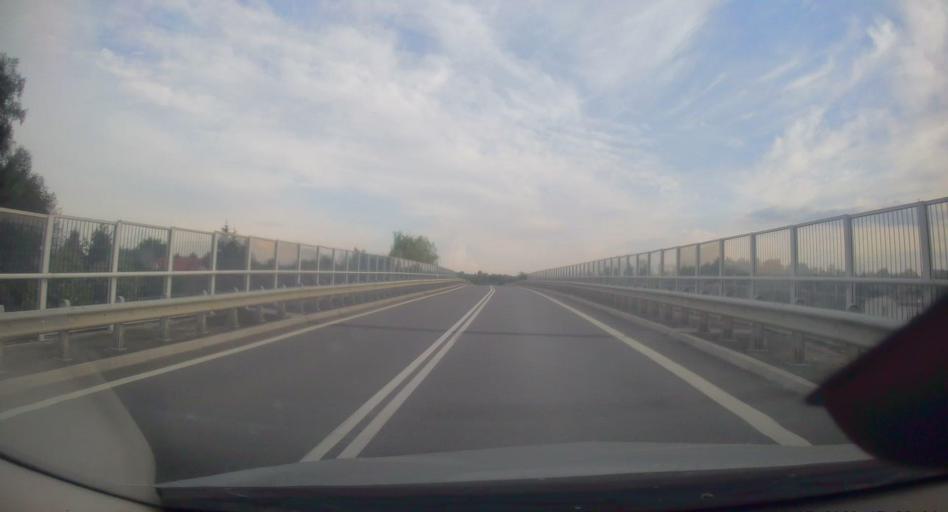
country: PL
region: Lesser Poland Voivodeship
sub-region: Powiat brzeski
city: Brzesko
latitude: 50.0032
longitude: 20.6009
